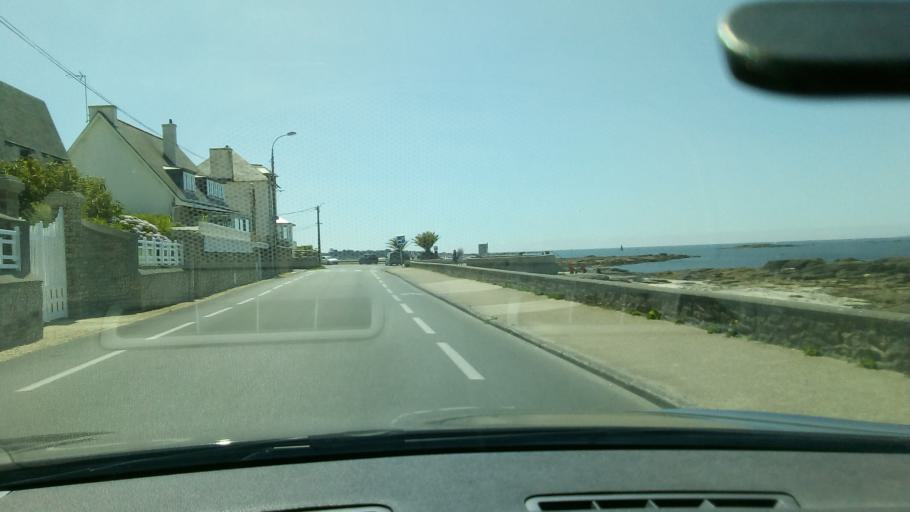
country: FR
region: Brittany
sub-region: Departement du Finistere
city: Concarneau
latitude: 47.8722
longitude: -3.9305
